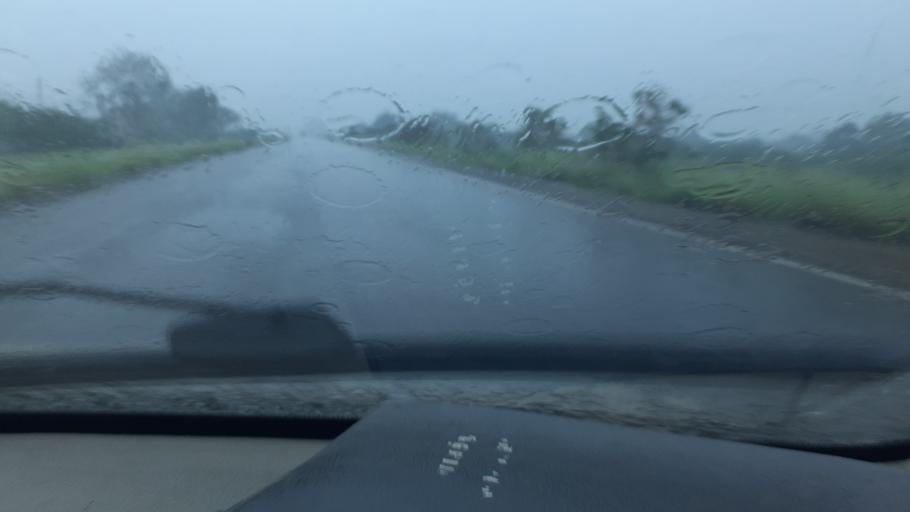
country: IN
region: Tamil Nadu
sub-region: Virudhunagar
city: Sattur
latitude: 9.4443
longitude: 77.9262
